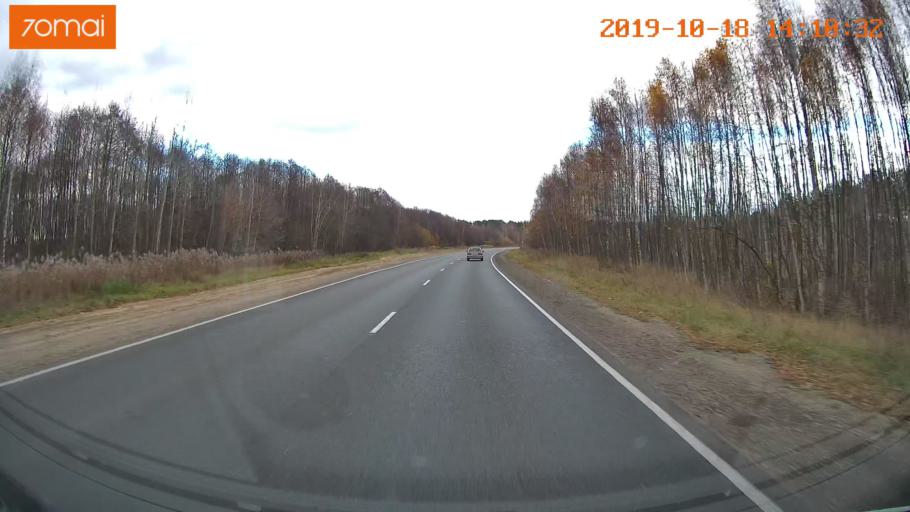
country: RU
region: Rjazan
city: Spas-Klepiki
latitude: 55.1416
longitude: 40.2100
